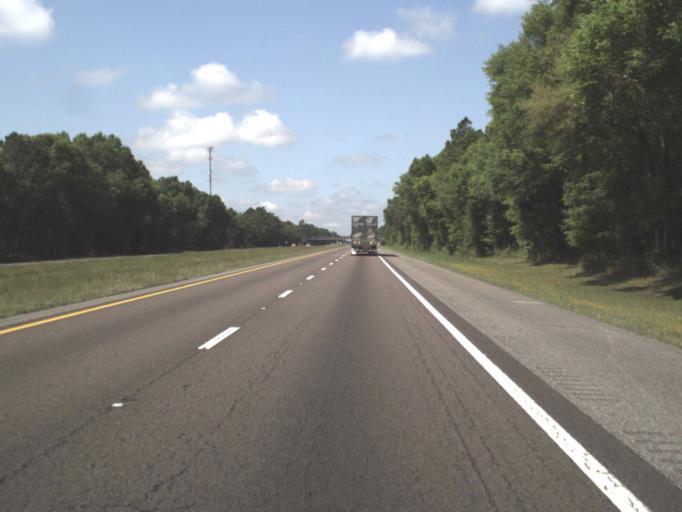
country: US
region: Florida
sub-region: Santa Rosa County
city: East Milton
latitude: 30.6595
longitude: -86.8713
